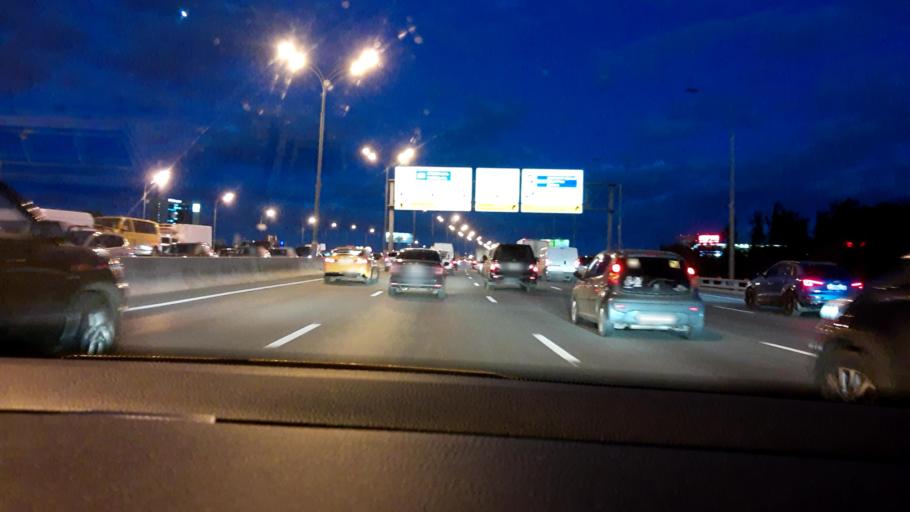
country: RU
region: Moscow
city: Vagonoremont
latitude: 55.9079
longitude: 37.5319
